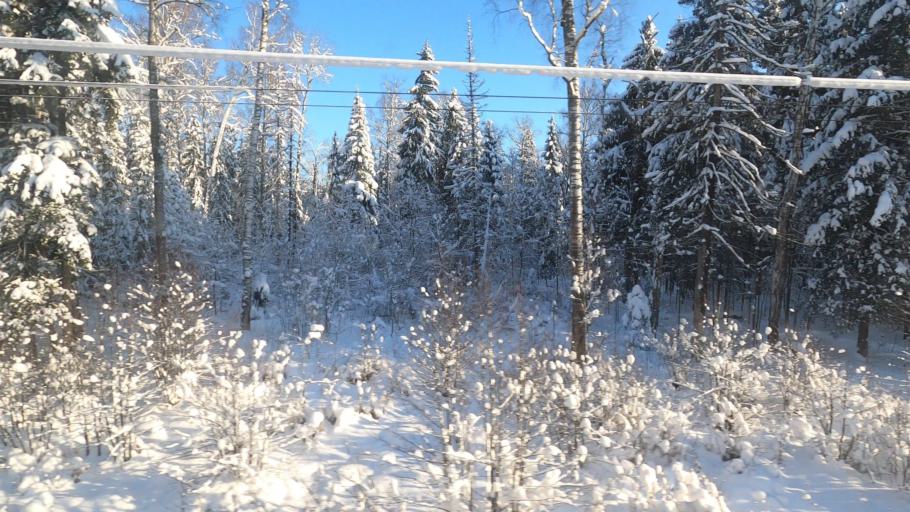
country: RU
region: Moskovskaya
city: Zhukovka
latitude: 56.4984
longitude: 37.5524
